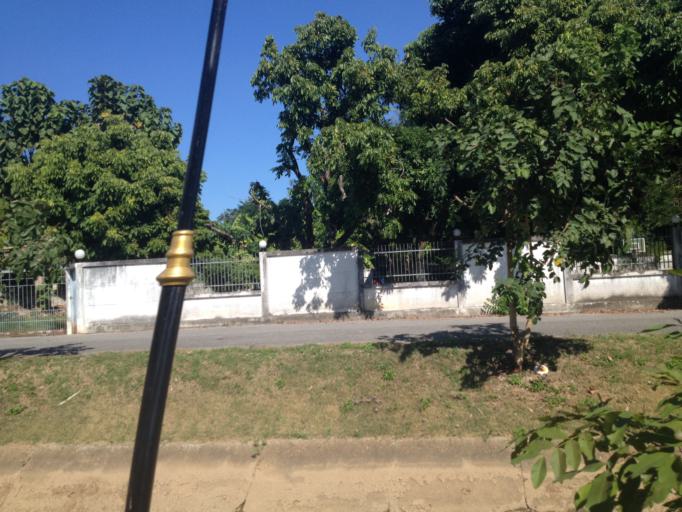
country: TH
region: Chiang Mai
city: Hang Dong
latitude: 18.6926
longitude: 98.9283
